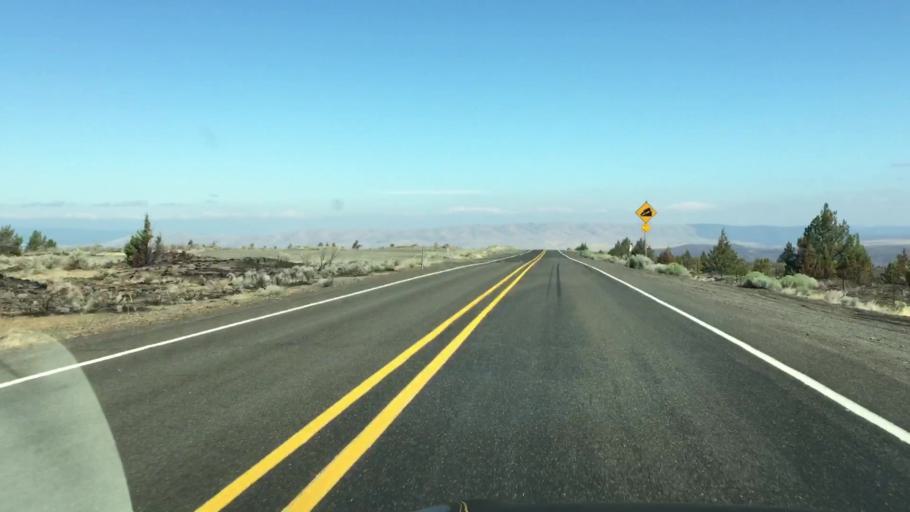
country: US
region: Oregon
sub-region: Jefferson County
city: Warm Springs
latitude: 45.0846
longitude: -121.0263
